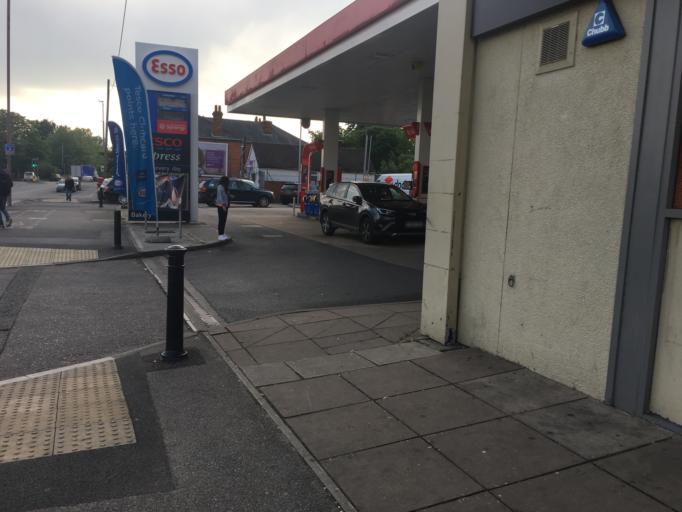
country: GB
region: England
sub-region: West Berkshire
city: Tilehurst
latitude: 51.4444
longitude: -1.0175
